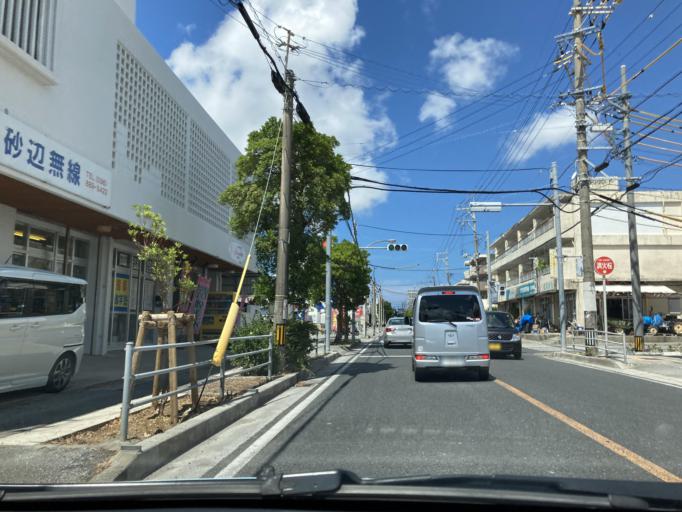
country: JP
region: Okinawa
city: Tomigusuku
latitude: 26.1817
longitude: 127.7150
